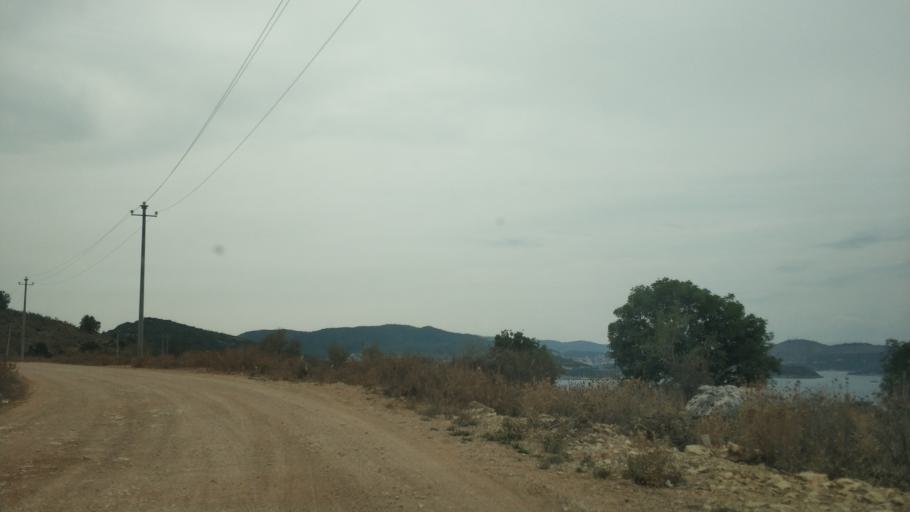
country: AL
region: Vlore
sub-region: Rrethi i Sarandes
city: Sarande
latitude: 39.7947
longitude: 20.0035
